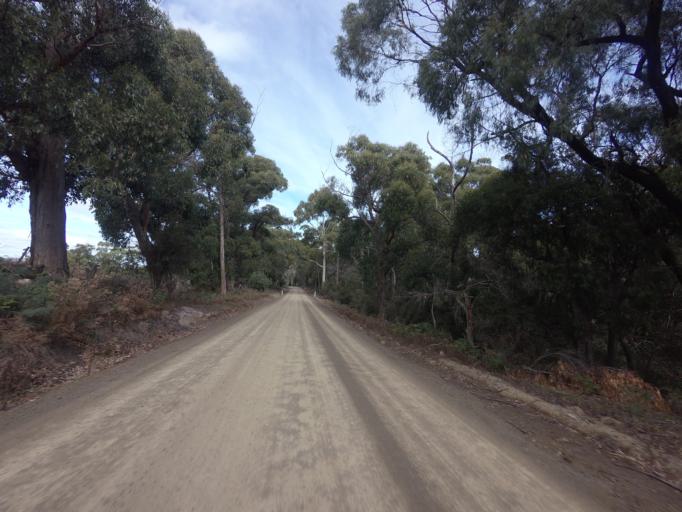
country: AU
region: Tasmania
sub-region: Clarence
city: Sandford
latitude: -43.0903
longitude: 147.7149
